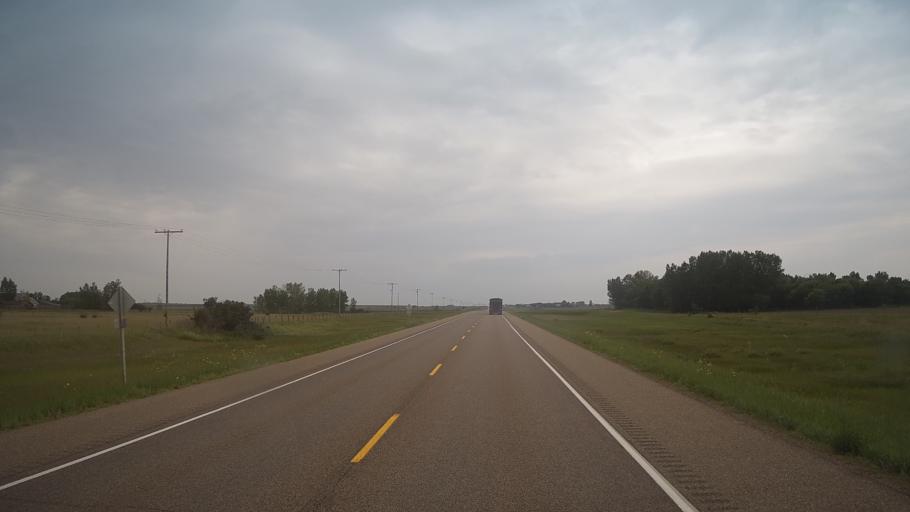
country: CA
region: Saskatchewan
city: Langham
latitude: 52.1289
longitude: -107.1405
